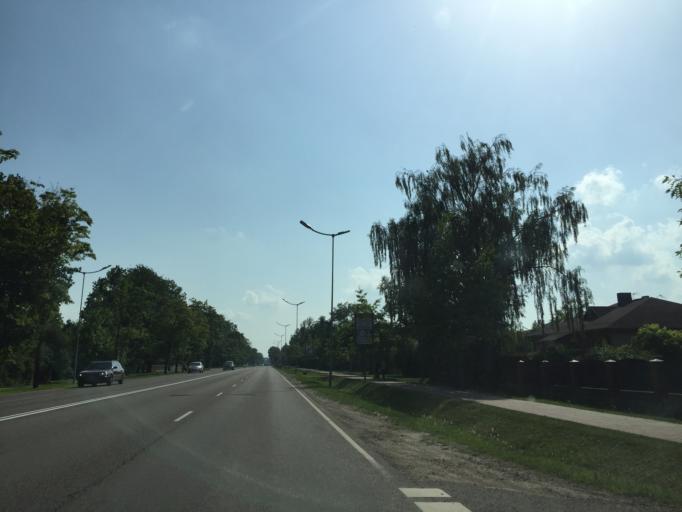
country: LV
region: Ozolnieku
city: Ozolnieki
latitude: 56.6658
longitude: 23.7554
